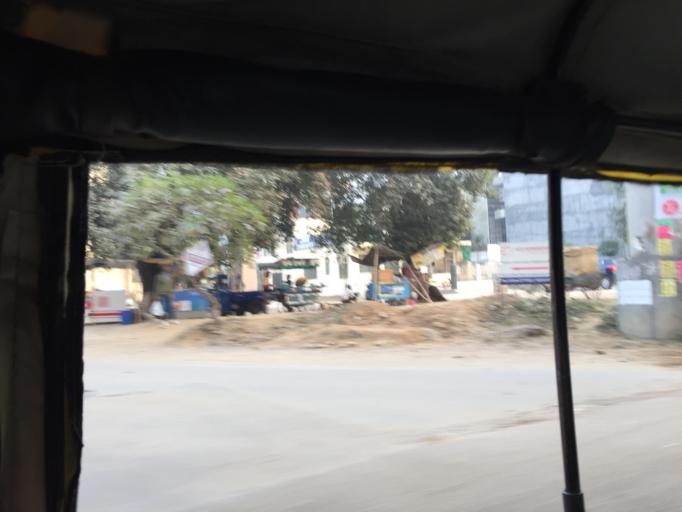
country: IN
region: Haryana
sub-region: Gurgaon
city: Gurgaon
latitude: 28.4281
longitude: 77.1054
